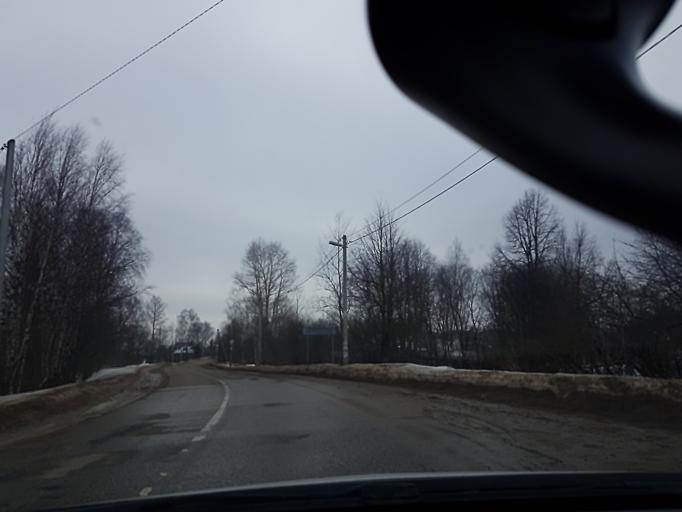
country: RU
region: Moskovskaya
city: Sychevo
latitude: 55.9926
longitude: 36.2242
